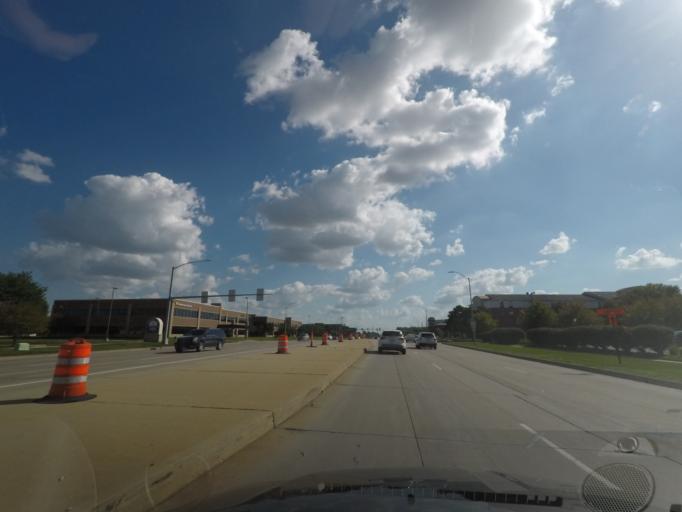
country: US
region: Iowa
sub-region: Dallas County
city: Waukee
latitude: 41.5889
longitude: -93.8093
